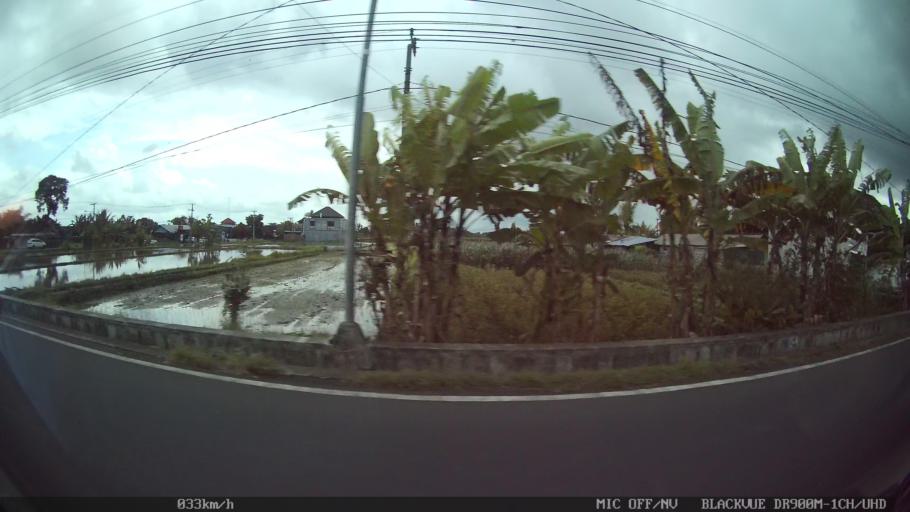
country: ID
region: Bali
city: Banjar Mambalkajanan
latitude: -8.5471
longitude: 115.2220
